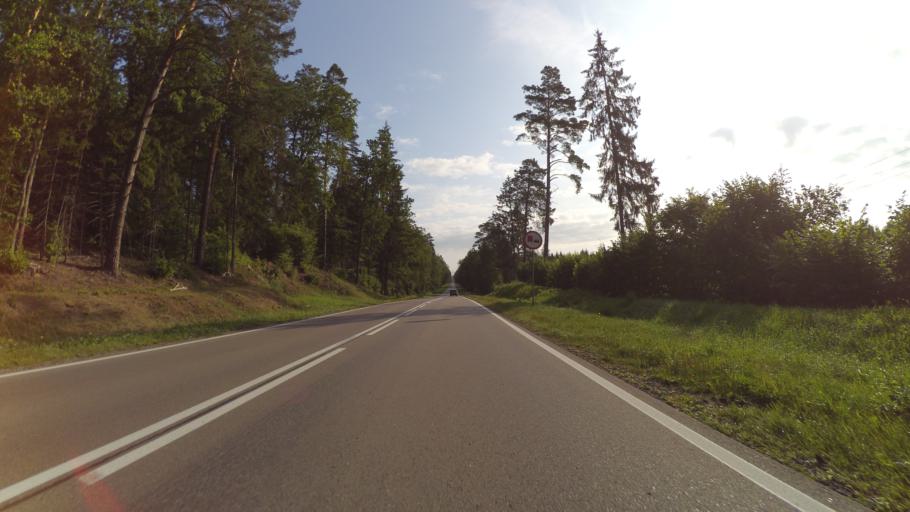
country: PL
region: Podlasie
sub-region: Powiat bialostocki
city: Czarna Bialostocka
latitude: 53.3169
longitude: 23.3325
